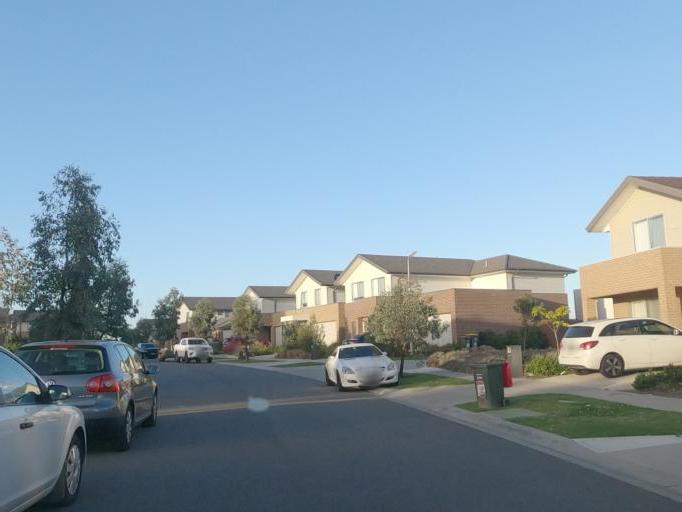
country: AU
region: Victoria
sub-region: Hume
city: Broadmeadows
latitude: -37.6740
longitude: 144.9067
